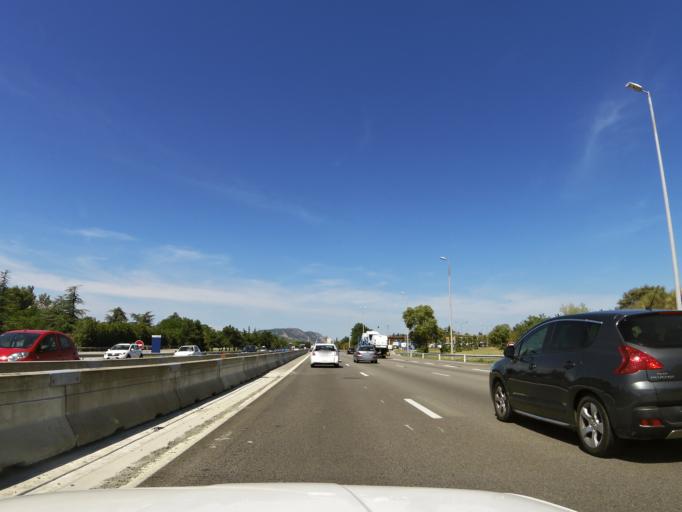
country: FR
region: Rhone-Alpes
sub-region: Departement de la Drome
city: Portes-les-Valence
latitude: 44.8632
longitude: 4.8664
